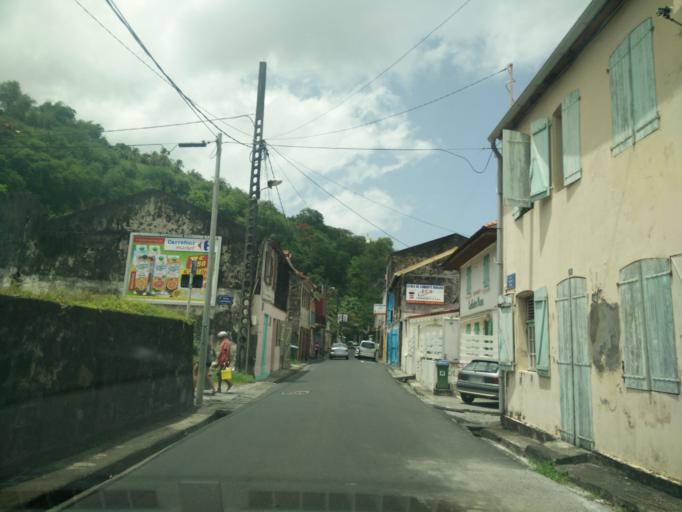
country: MQ
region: Martinique
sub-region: Martinique
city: Saint-Pierre
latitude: 14.7385
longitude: -61.1764
